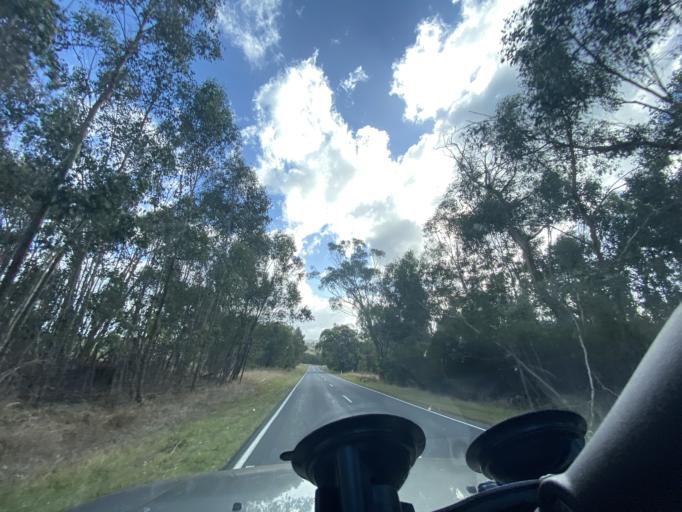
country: AU
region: Victoria
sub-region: Murrindindi
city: Kinglake West
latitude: -37.3224
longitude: 145.3057
